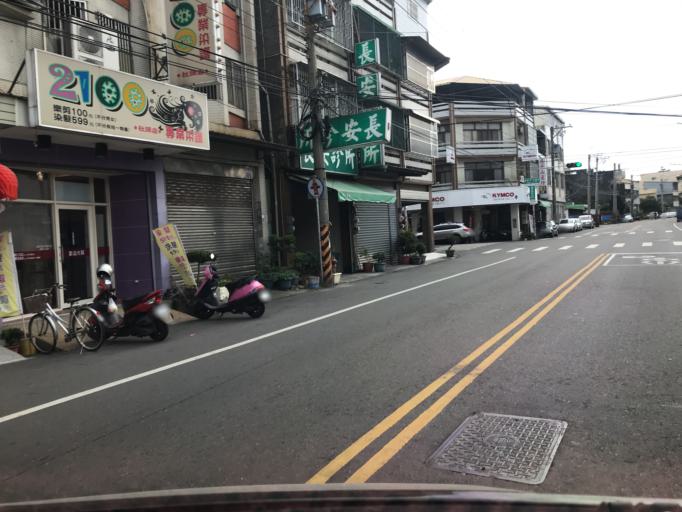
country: TW
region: Taiwan
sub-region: Nantou
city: Nantou
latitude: 23.8950
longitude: 120.5883
